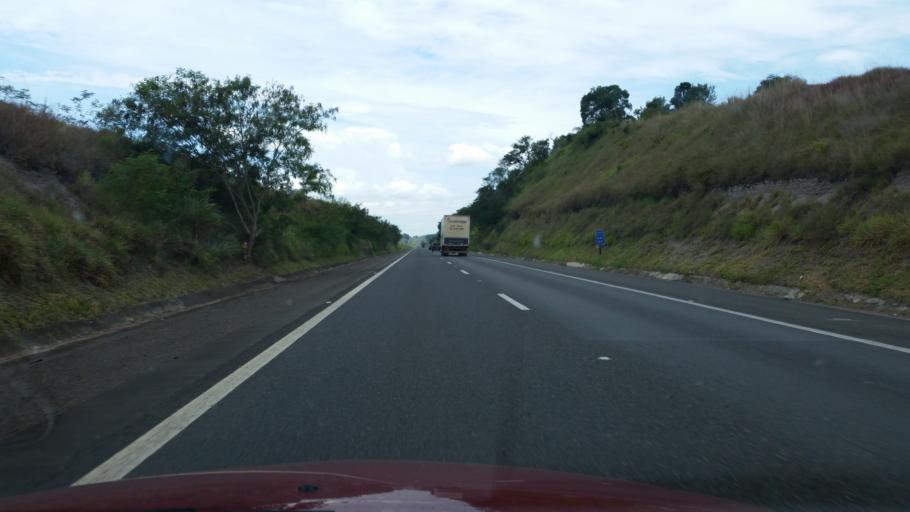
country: BR
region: Sao Paulo
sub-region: Porangaba
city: Porangaba
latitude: -23.2345
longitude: -48.1388
